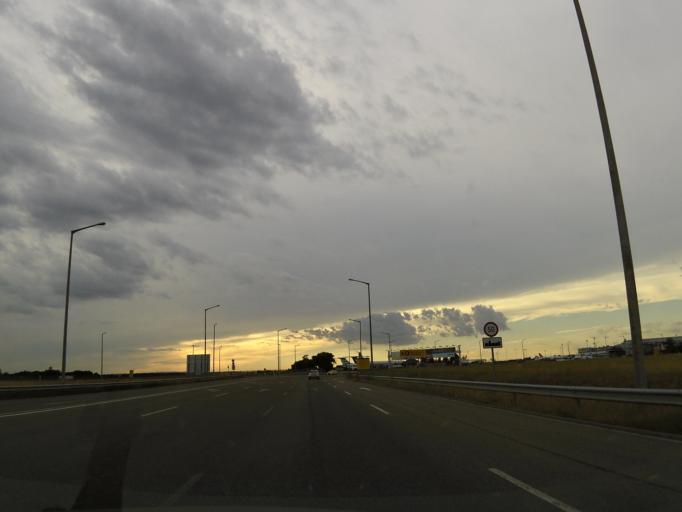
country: HU
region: Pest
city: Vecses
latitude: 47.4249
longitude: 19.2641
